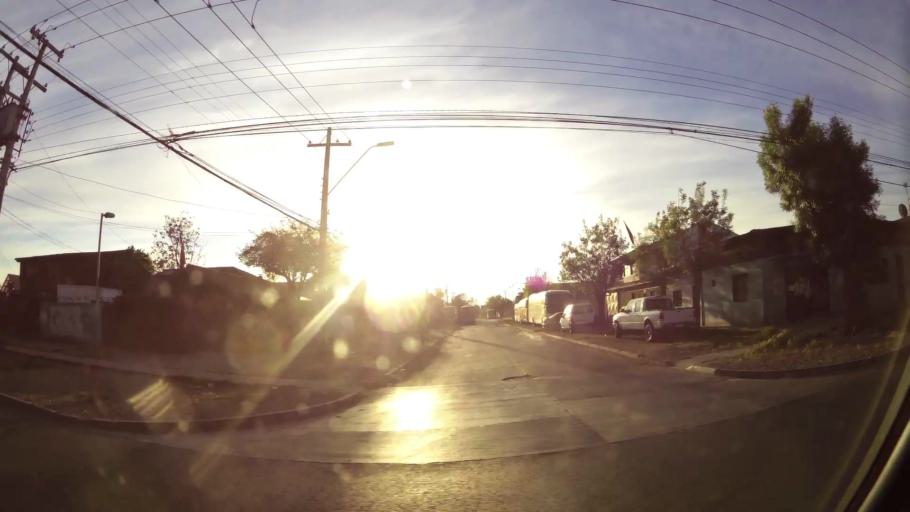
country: CL
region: Santiago Metropolitan
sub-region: Provincia de Santiago
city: Lo Prado
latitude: -33.4268
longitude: -70.7193
